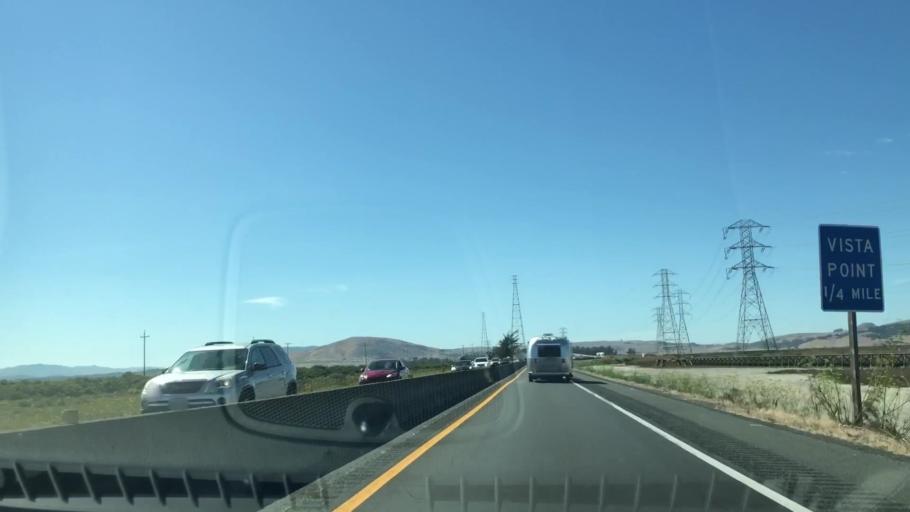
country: US
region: California
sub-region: Marin County
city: Black Point-Green Point
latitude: 38.1541
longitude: -122.3958
